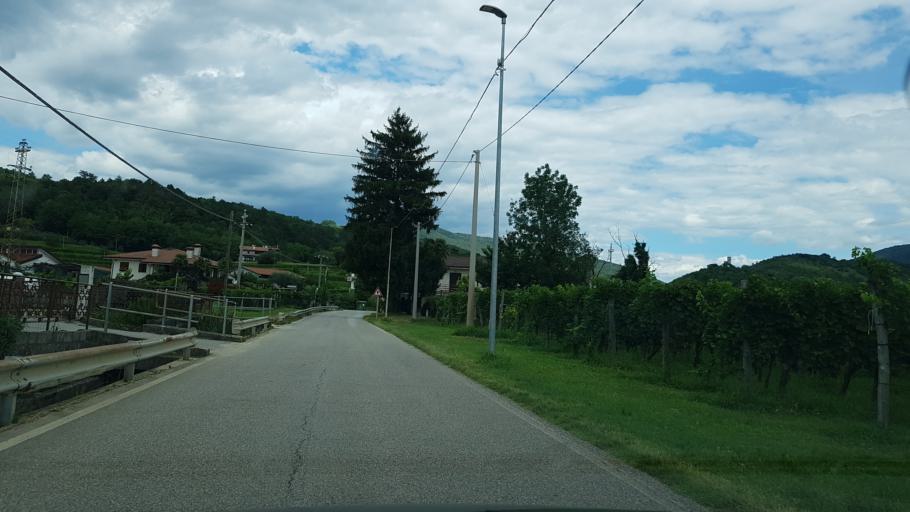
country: IT
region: Friuli Venezia Giulia
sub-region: Provincia di Udine
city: Prepotto
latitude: 46.0528
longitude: 13.4885
